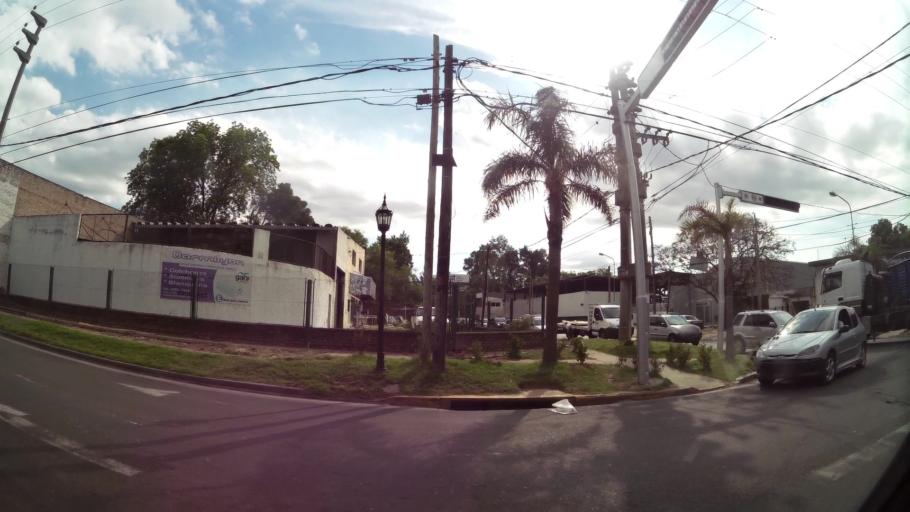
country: AR
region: Buenos Aires
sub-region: Partido de Tigre
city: Tigre
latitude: -34.4764
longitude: -58.6249
